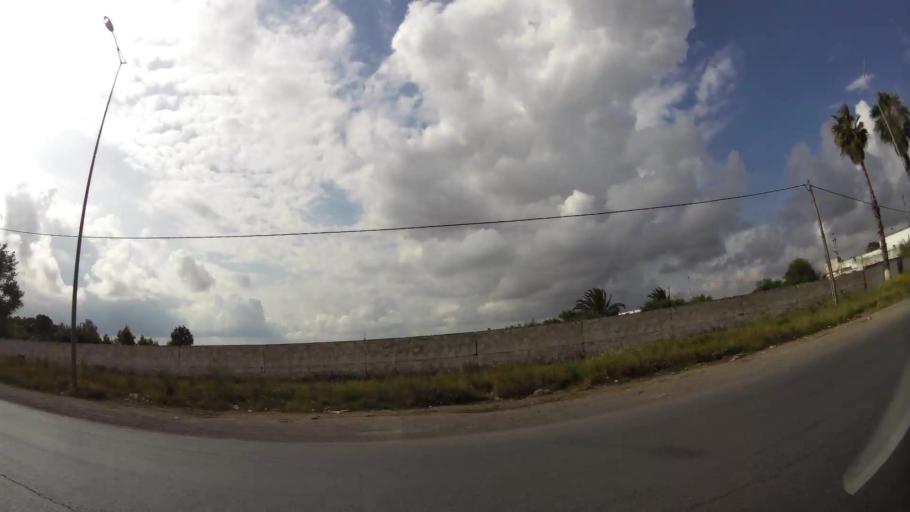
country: MA
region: Gharb-Chrarda-Beni Hssen
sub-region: Kenitra Province
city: Kenitra
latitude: 34.2810
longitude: -6.5388
